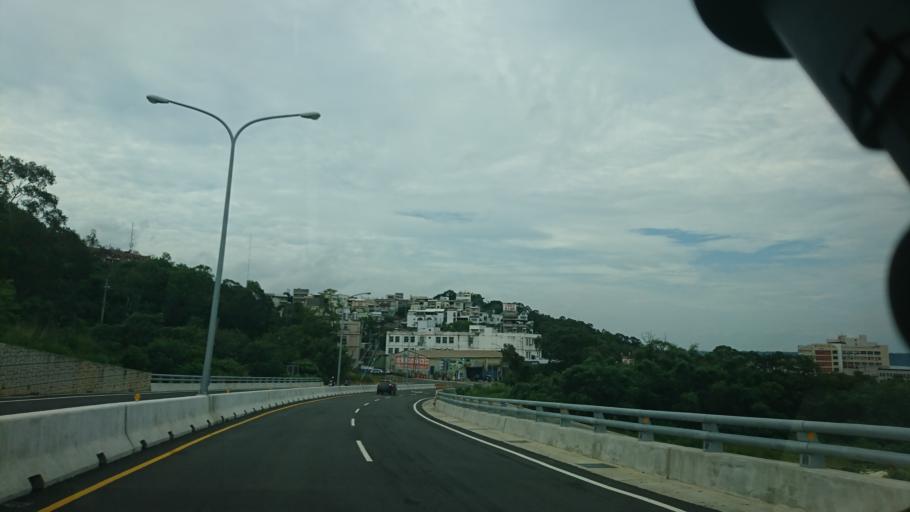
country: TW
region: Taiwan
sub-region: Miaoli
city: Miaoli
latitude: 24.5415
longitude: 120.8091
